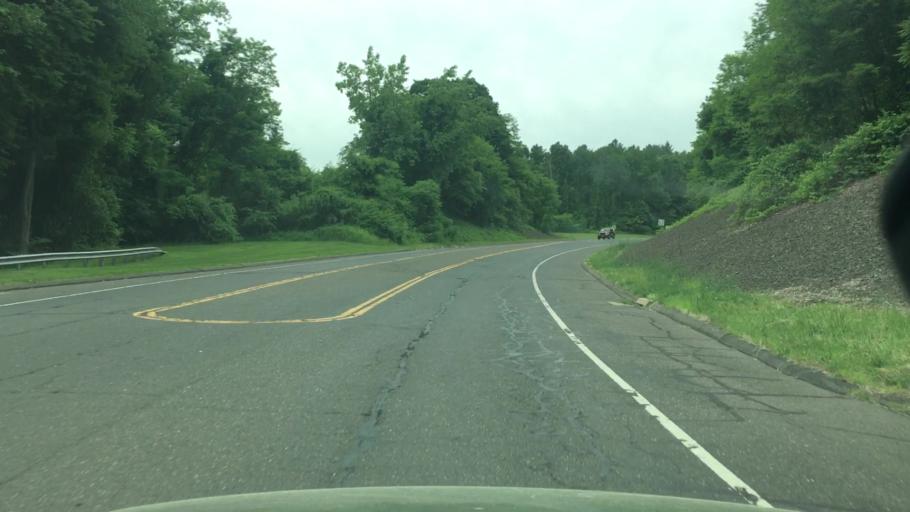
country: US
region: Connecticut
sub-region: Hartford County
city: Windsor Locks
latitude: 41.8990
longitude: -72.6339
